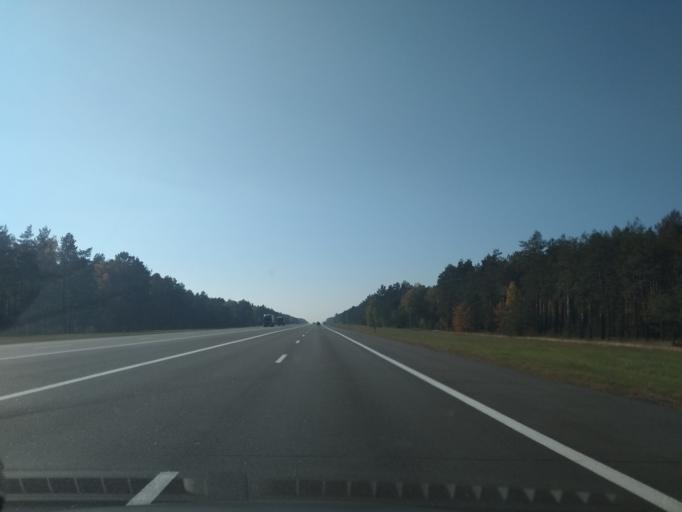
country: BY
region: Brest
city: Ivatsevichy
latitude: 52.7628
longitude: 25.5234
